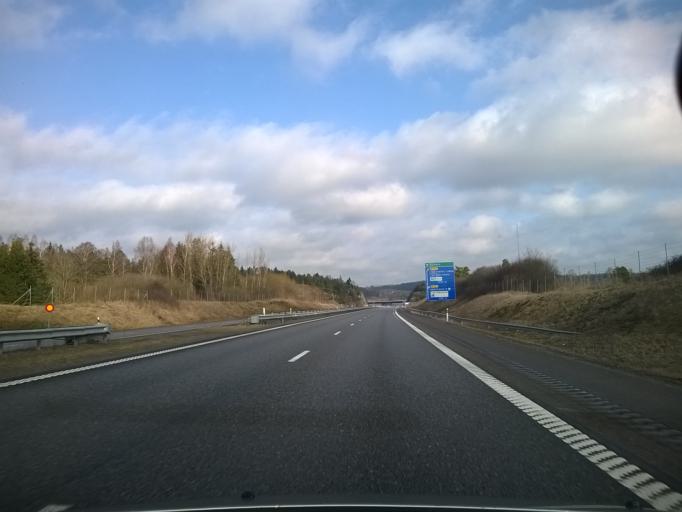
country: SE
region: Vaestra Goetaland
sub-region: Uddevalla Kommun
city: Uddevalla
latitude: 58.3437
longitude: 11.8233
